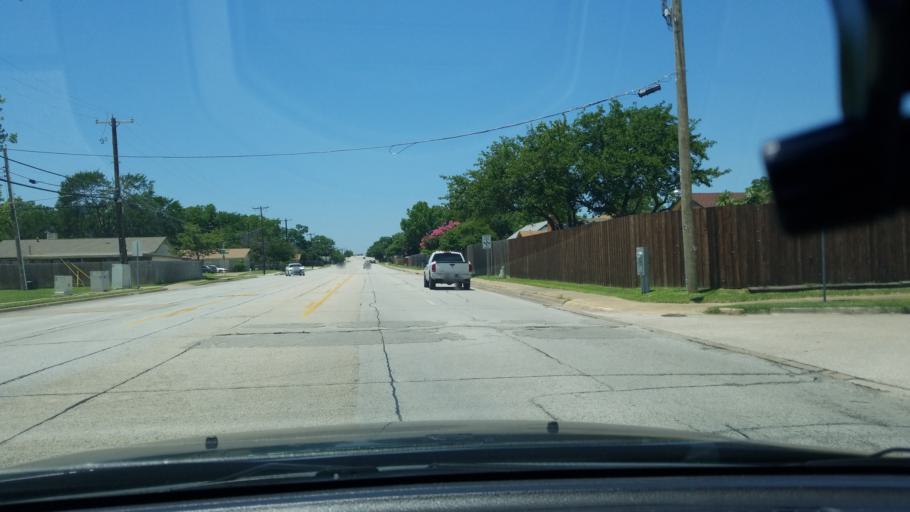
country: US
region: Texas
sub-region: Dallas County
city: Mesquite
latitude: 32.8053
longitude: -96.6494
